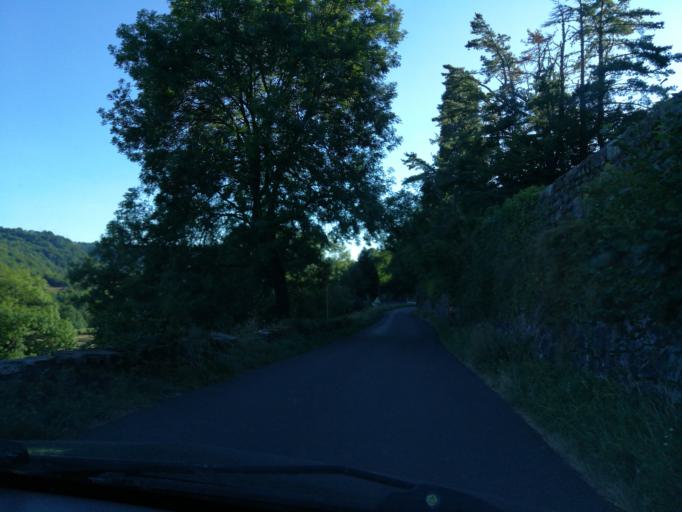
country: FR
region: Auvergne
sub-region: Departement du Cantal
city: Saint-Cernin
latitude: 45.1405
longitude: 2.5079
